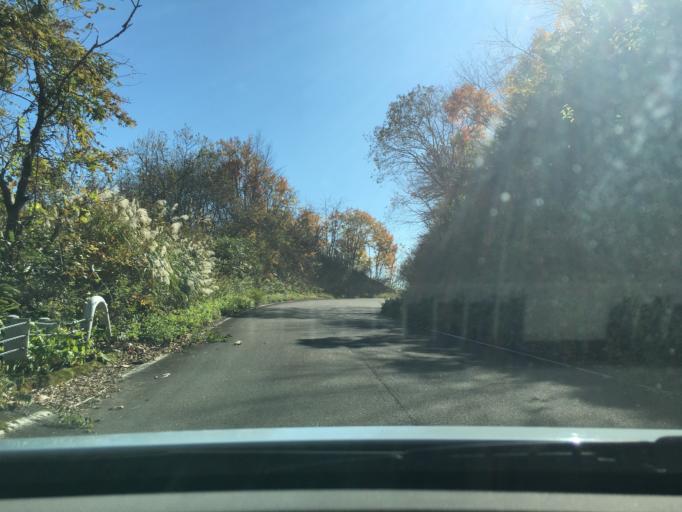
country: JP
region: Fukushima
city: Inawashiro
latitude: 37.4040
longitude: 140.0236
